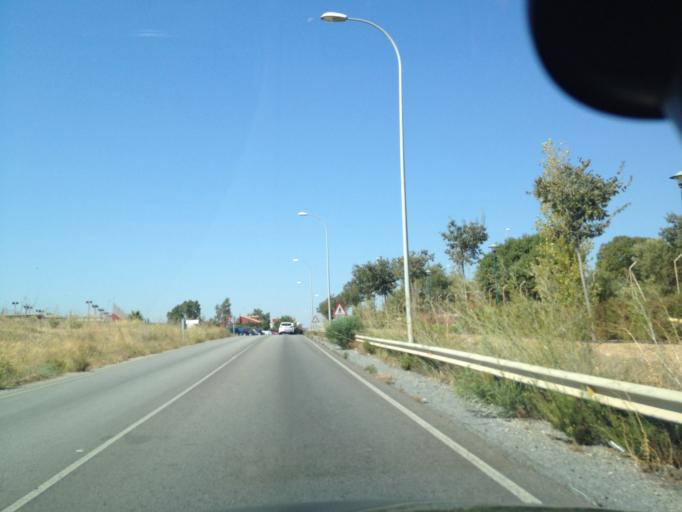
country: ES
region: Andalusia
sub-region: Provincia de Malaga
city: Estacion de Cartama
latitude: 36.7327
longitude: -4.5578
